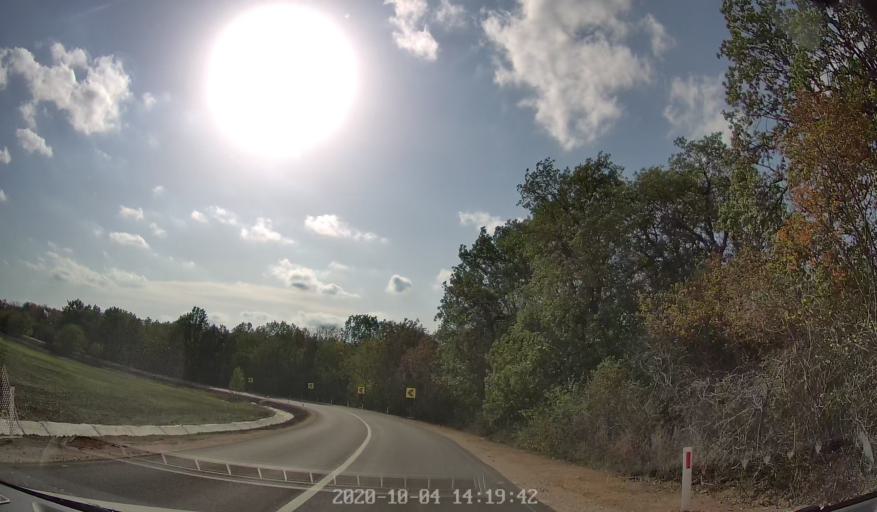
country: MD
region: Rezina
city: Saharna
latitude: 47.5893
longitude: 28.9709
